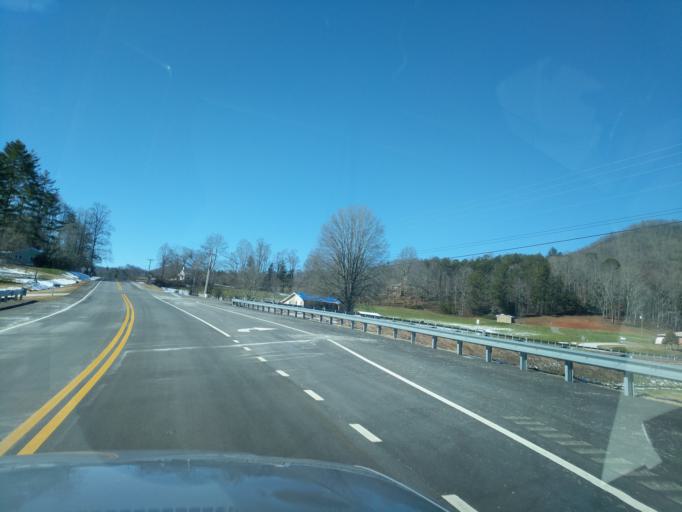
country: US
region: Georgia
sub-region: Towns County
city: Hiawassee
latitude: 34.9290
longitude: -83.6467
